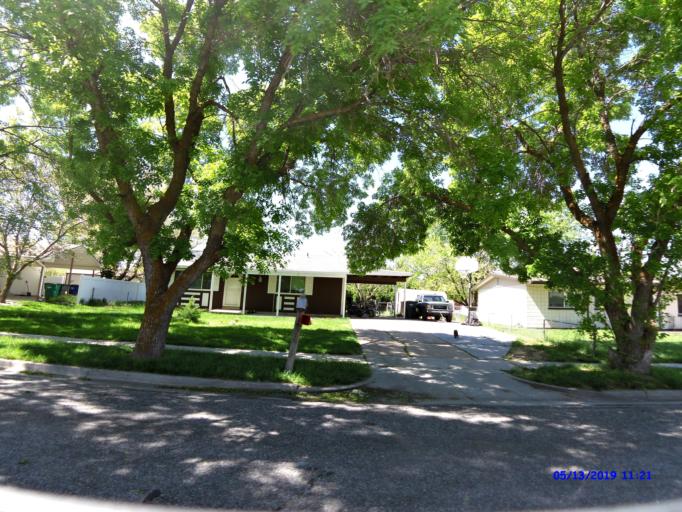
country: US
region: Utah
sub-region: Weber County
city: North Ogden
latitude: 41.2815
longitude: -111.9623
